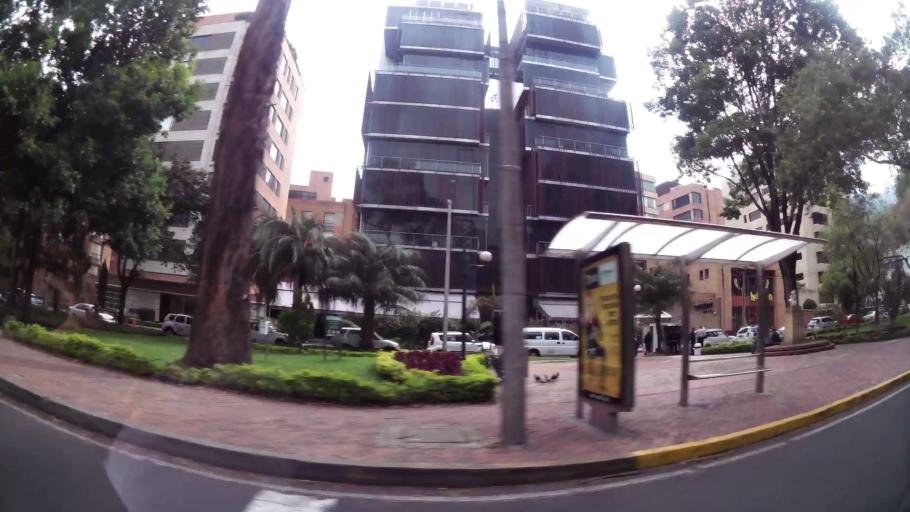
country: CO
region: Bogota D.C.
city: Barrio San Luis
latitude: 4.6656
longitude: -74.0509
